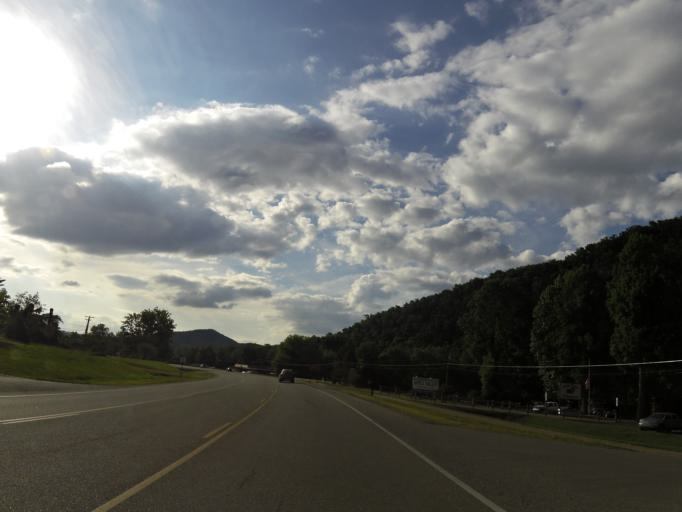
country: US
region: Tennessee
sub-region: Blount County
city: Wildwood
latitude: 35.6769
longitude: -83.7200
